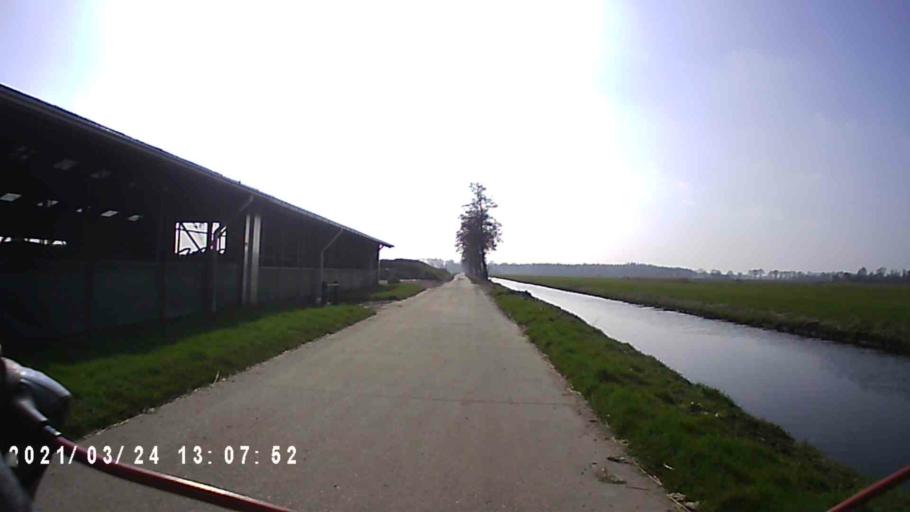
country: NL
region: Groningen
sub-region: Gemeente Leek
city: Leek
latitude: 53.1283
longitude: 6.3035
